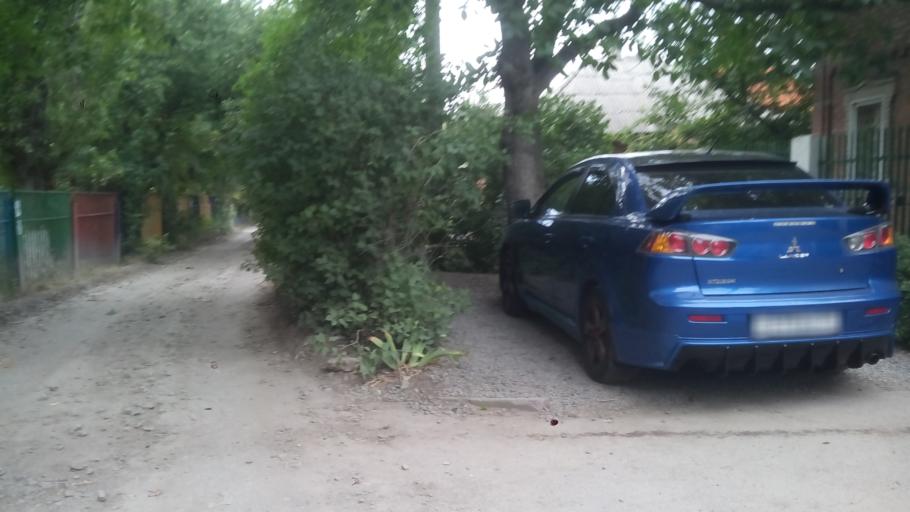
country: RU
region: Rostov
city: Rostov-na-Donu
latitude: 47.2292
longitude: 39.6350
